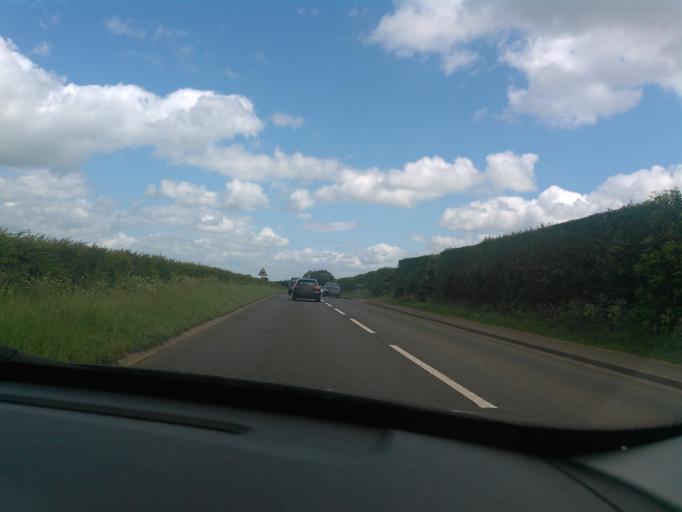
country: GB
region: England
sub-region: Shropshire
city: Stoke upon Tern
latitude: 52.8888
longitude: -2.5372
